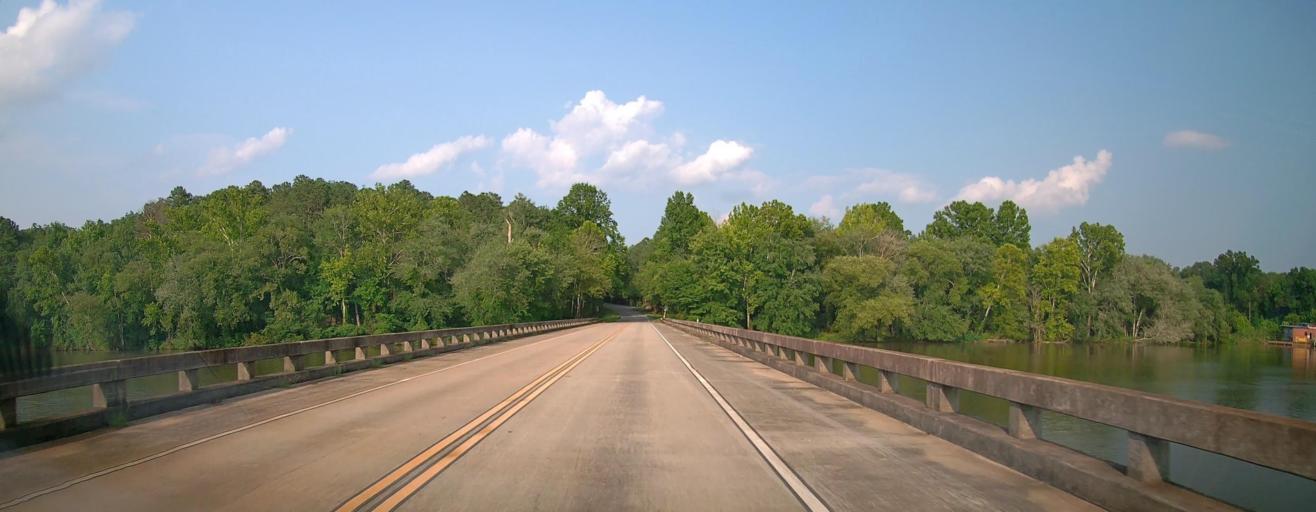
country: US
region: Georgia
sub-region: Monroe County
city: Forsyth
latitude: 33.1078
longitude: -83.7953
